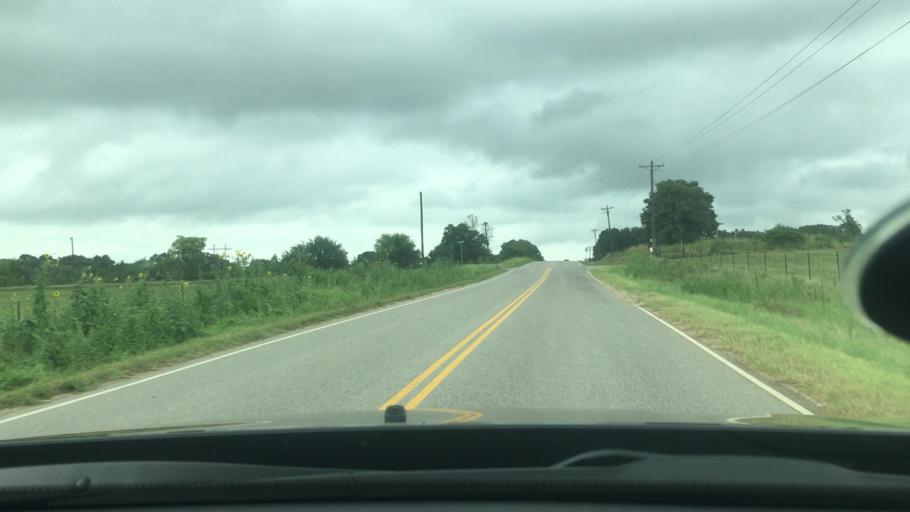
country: US
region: Oklahoma
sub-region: Bryan County
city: Calera
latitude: 33.9681
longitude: -96.5005
